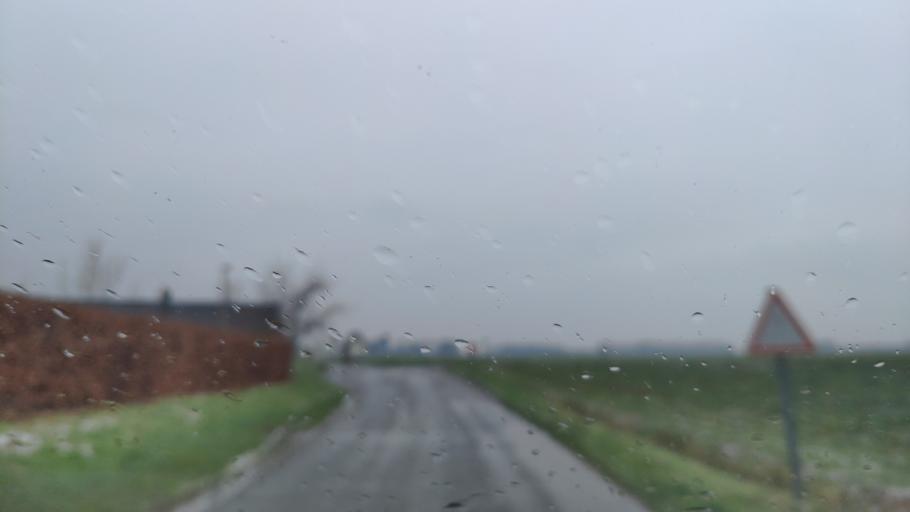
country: FR
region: Haute-Normandie
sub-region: Departement de la Seine-Maritime
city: Cany-Barville
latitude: 49.7942
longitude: 0.6790
